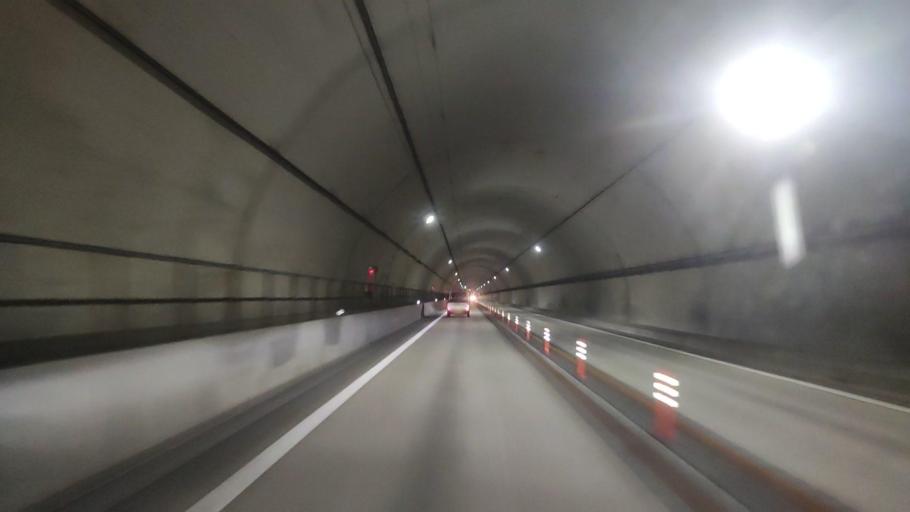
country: JP
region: Wakayama
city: Tanabe
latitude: 33.6016
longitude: 135.4314
